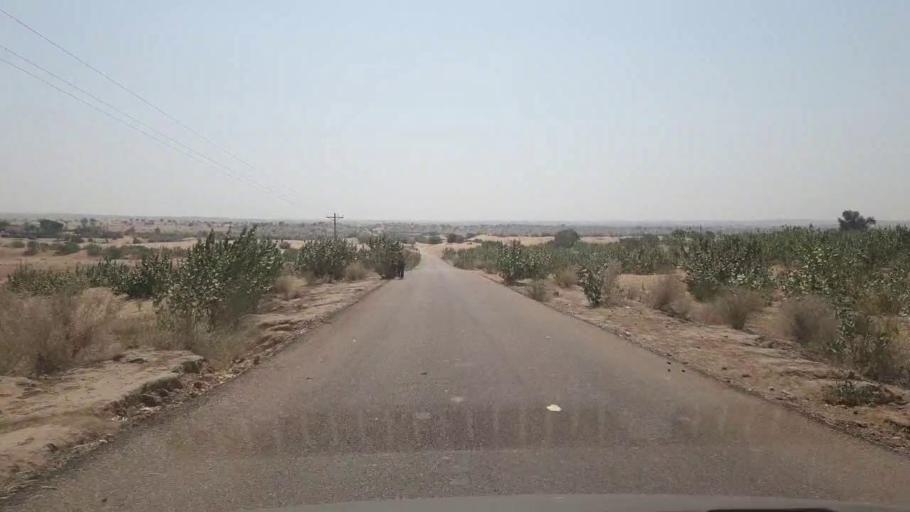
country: PK
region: Sindh
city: Chor
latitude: 25.6152
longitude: 70.1768
